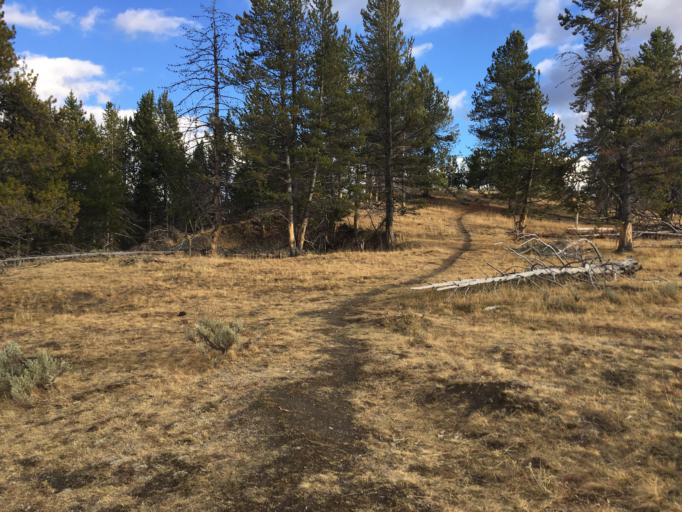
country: US
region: Montana
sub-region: Gallatin County
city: West Yellowstone
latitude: 44.6712
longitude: -110.4719
